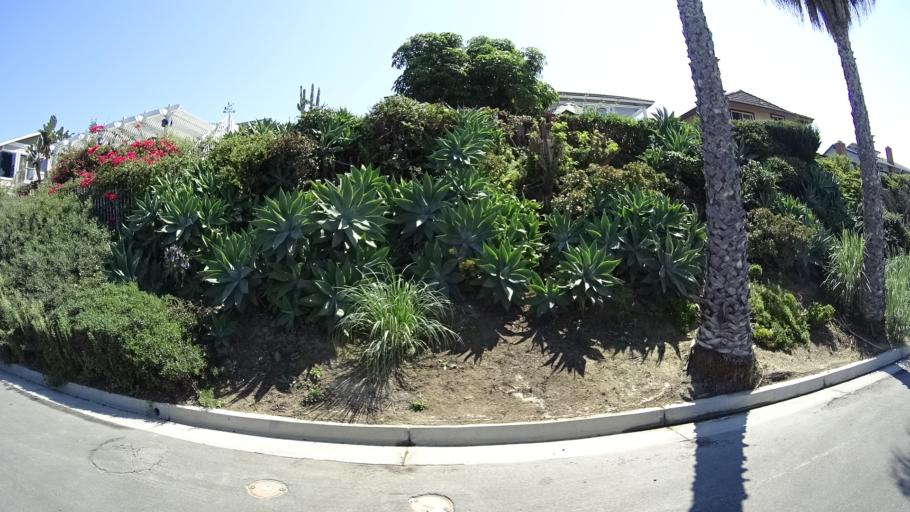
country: US
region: California
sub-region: Orange County
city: San Clemente
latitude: 33.4428
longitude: -117.6371
